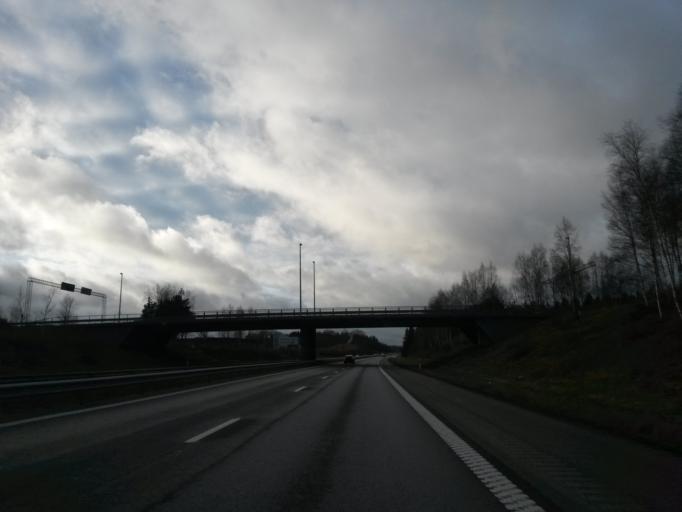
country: SE
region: Vaestra Goetaland
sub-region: Boras Kommun
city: Sjomarken
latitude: 57.6987
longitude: 12.8244
